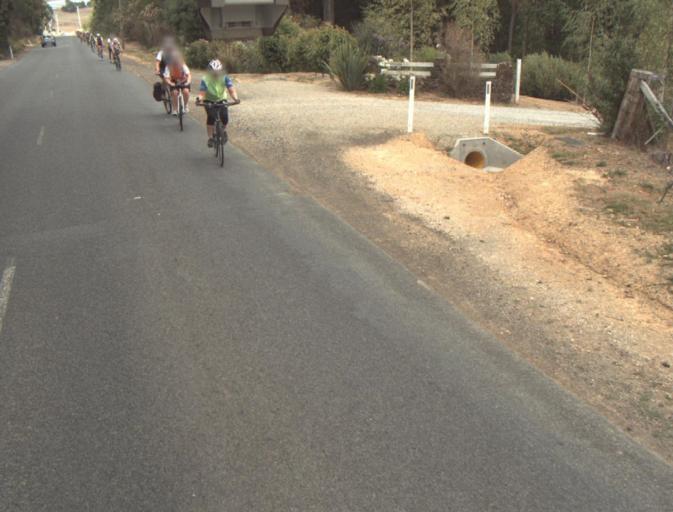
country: AU
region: Tasmania
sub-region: Launceston
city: Mayfield
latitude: -41.2166
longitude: 147.2093
